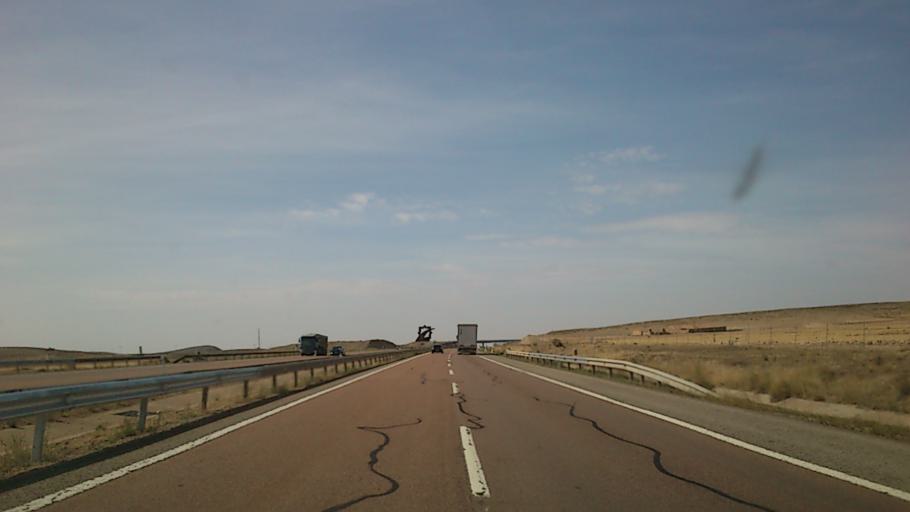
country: ES
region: Aragon
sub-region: Provincia de Teruel
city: Singra
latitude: 40.6339
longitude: -1.3094
